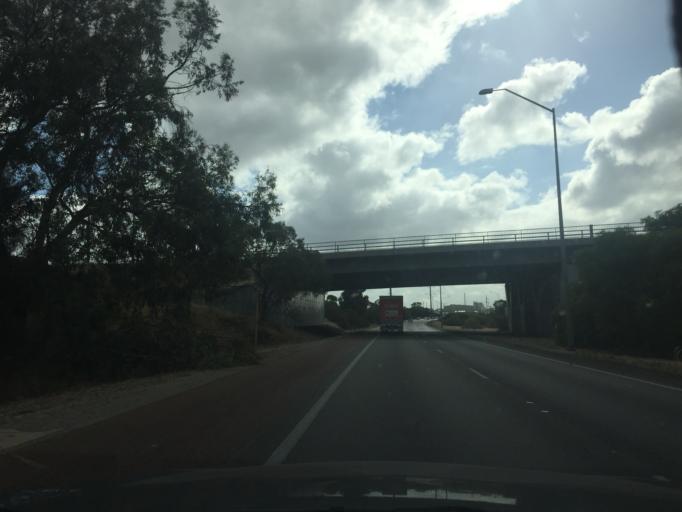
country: AU
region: Western Australia
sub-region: Canning
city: Canning Vale
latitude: -32.0536
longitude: 115.9322
